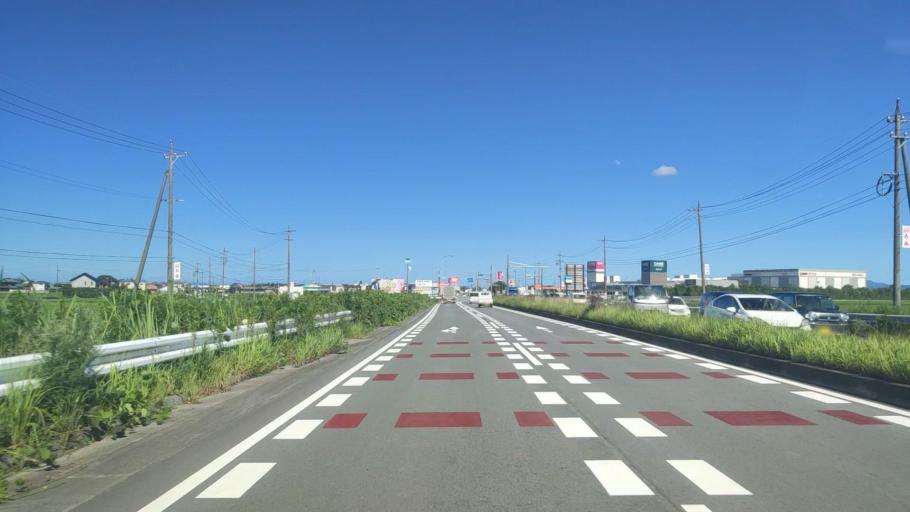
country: JP
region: Mie
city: Ise
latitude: 34.5848
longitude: 136.6087
